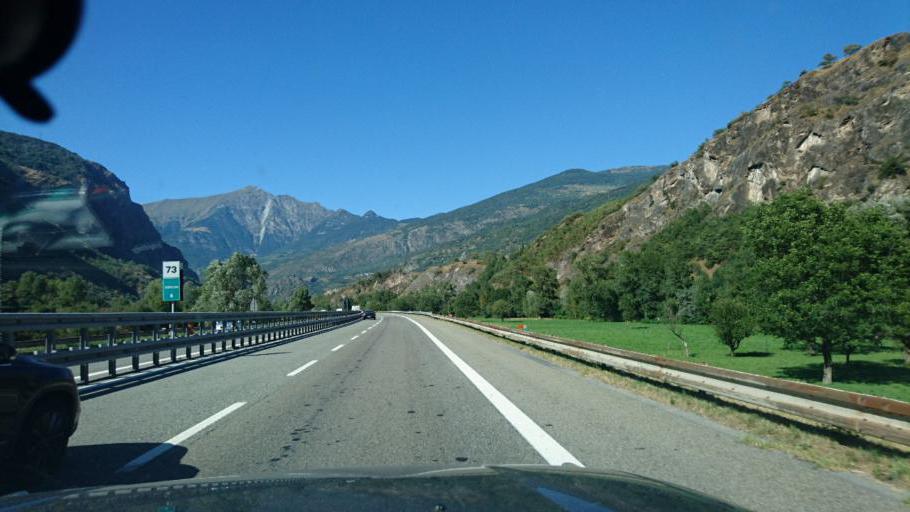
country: IT
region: Aosta Valley
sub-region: Valle d'Aosta
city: Champdepraz
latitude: 45.6914
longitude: 7.6683
